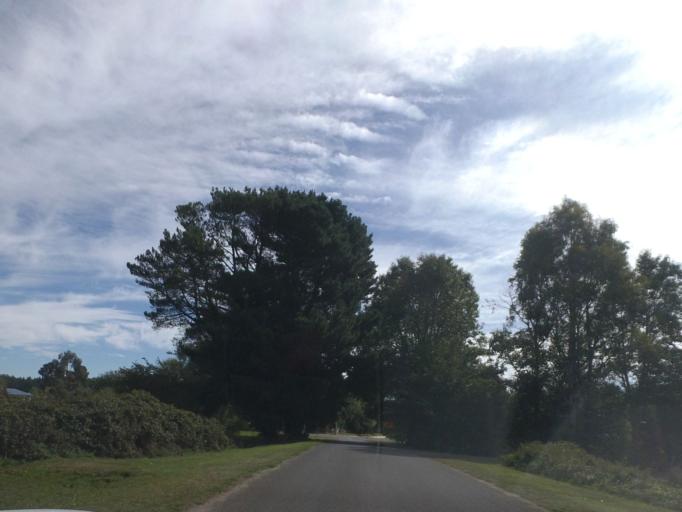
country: AU
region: Victoria
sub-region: Mount Alexander
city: Castlemaine
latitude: -37.3911
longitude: 144.2590
